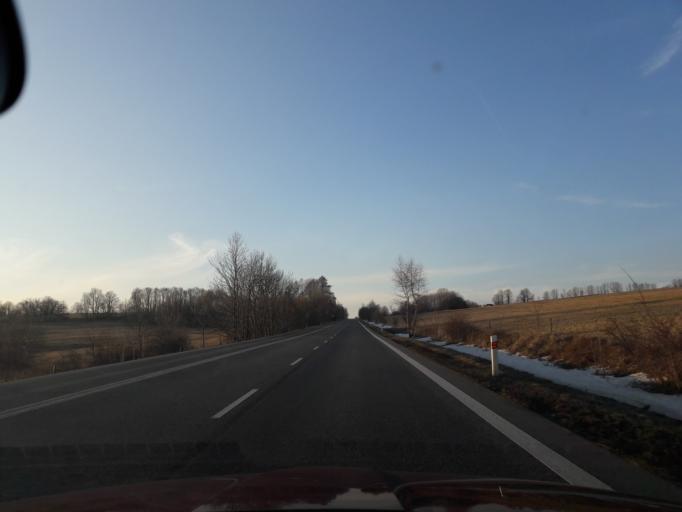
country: CZ
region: Ustecky
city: Dolni Podluzi
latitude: 50.8917
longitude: 14.5743
